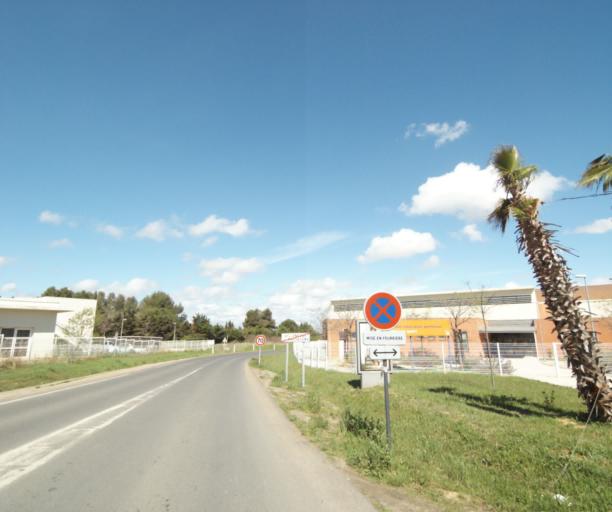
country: FR
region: Languedoc-Roussillon
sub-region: Departement de l'Herault
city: Villeneuve-les-Maguelone
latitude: 43.5330
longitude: 3.8525
